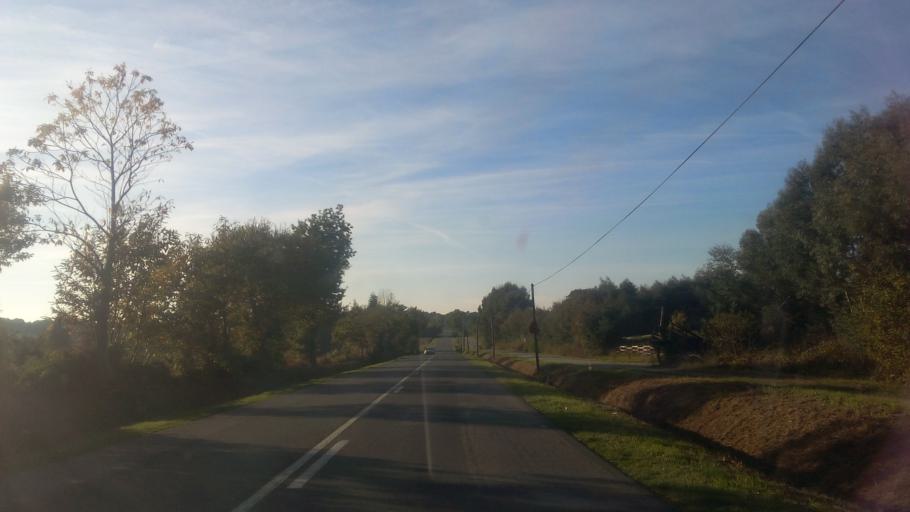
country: FR
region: Brittany
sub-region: Departement du Morbihan
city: Questembert
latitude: 47.6933
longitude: -2.4914
